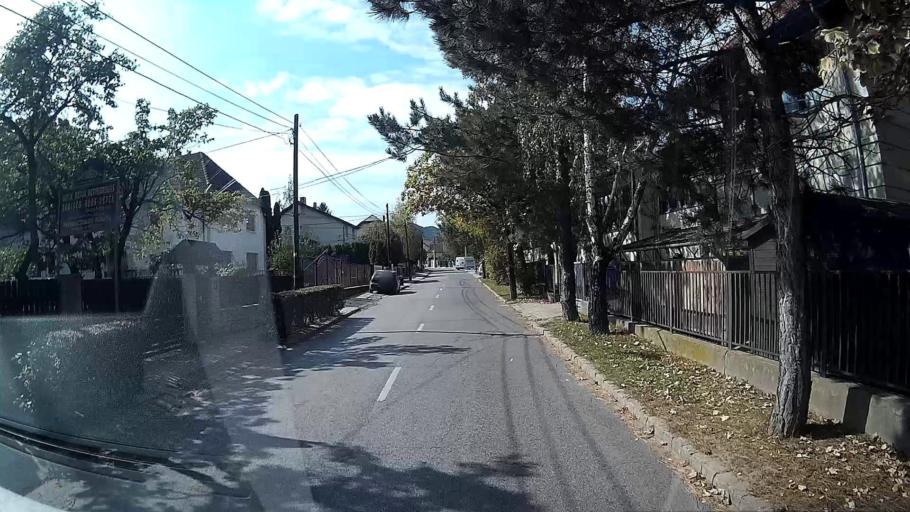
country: HU
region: Pest
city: Solymar
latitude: 47.5906
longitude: 18.9289
